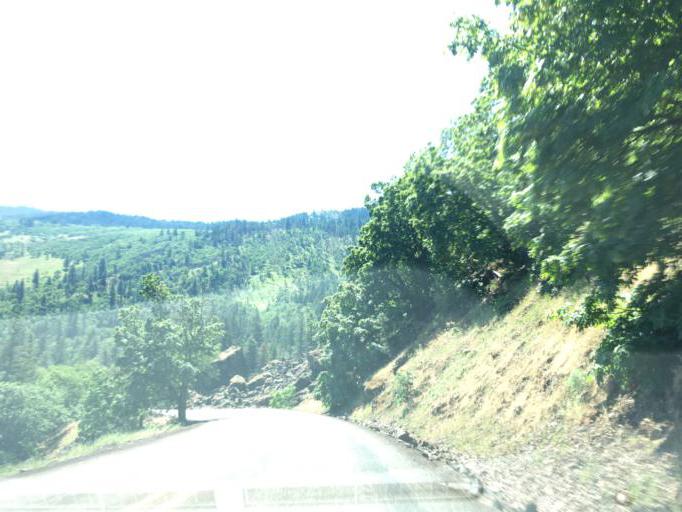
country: US
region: Oregon
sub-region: Wasco County
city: Chenoweth
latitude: 45.6787
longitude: -121.2989
